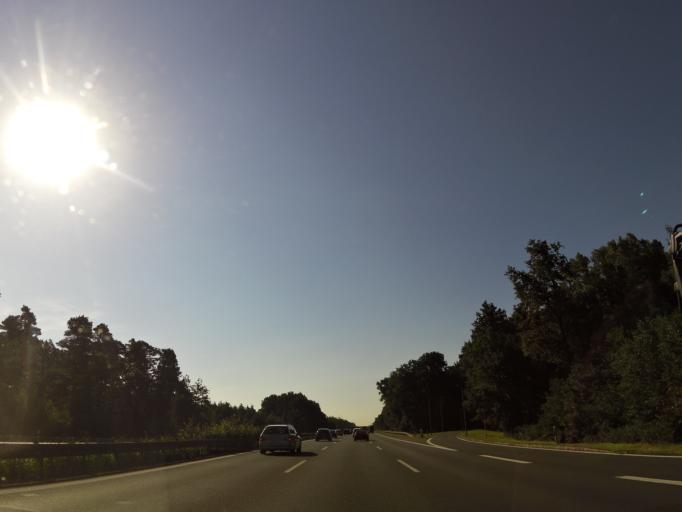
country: DE
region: Bavaria
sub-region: Regierungsbezirk Mittelfranken
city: Wetzendorf
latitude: 49.5279
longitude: 11.0638
